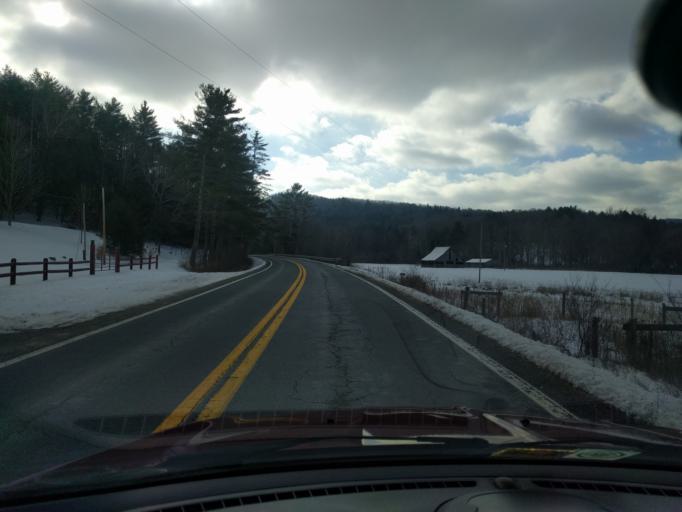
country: US
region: West Virginia
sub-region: Pocahontas County
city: Marlinton
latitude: 38.1488
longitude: -79.9830
